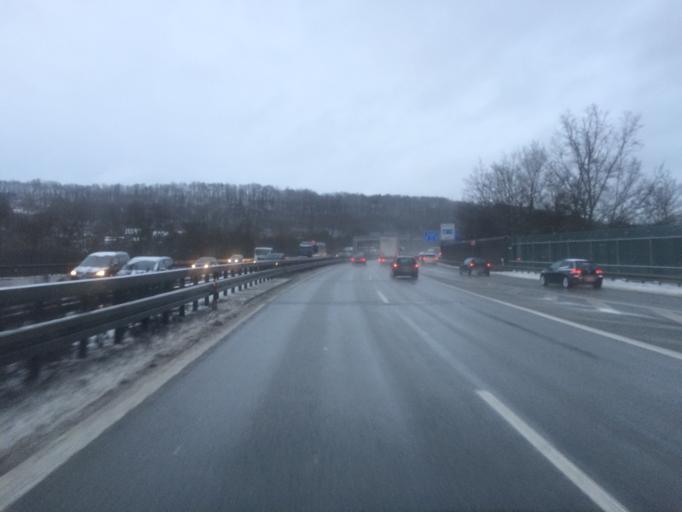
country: DE
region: Bavaria
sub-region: Upper Palatinate
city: Lappersdorf
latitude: 49.0260
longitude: 12.0708
